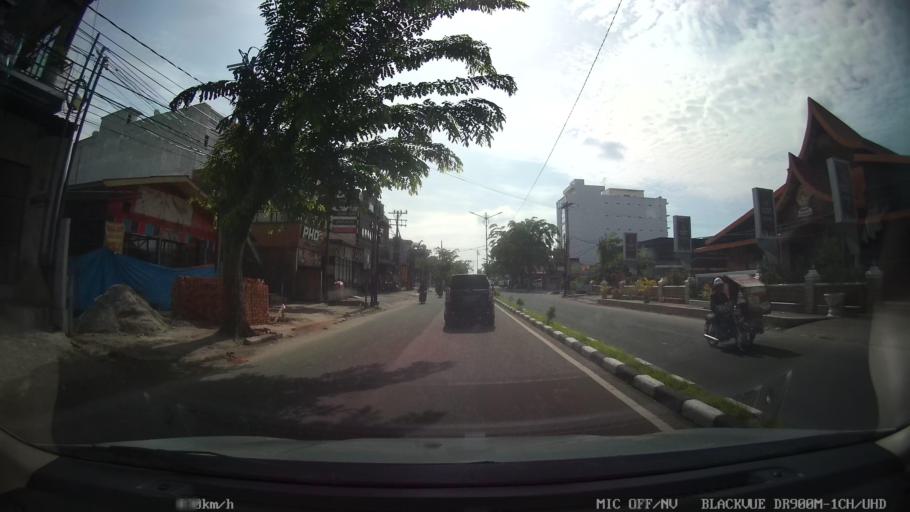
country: ID
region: North Sumatra
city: Medan
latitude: 3.5676
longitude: 98.6460
